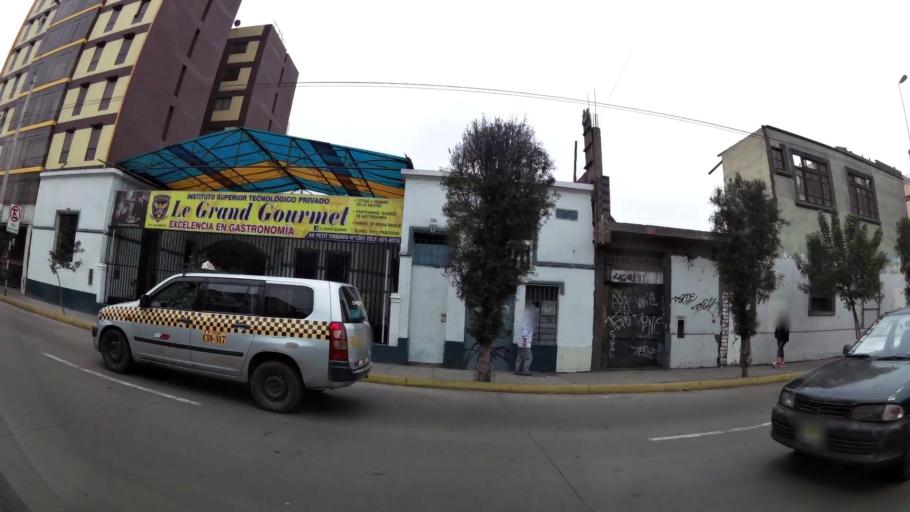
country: PE
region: Lima
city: Lima
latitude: -12.0772
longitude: -77.0344
